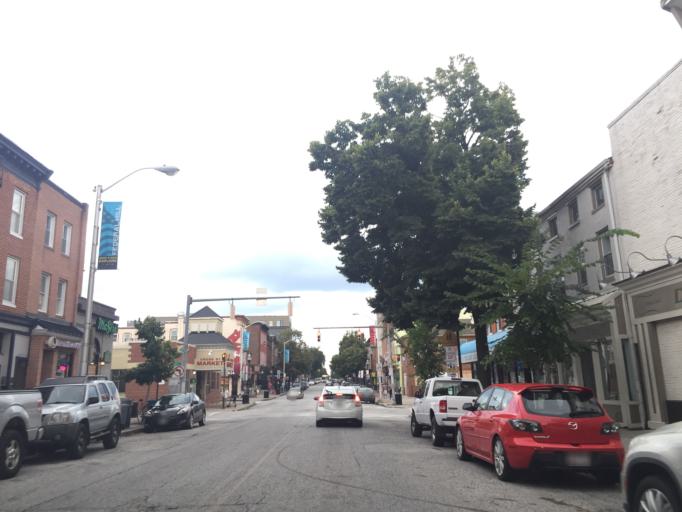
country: US
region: Maryland
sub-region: City of Baltimore
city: Baltimore
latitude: 39.2772
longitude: -76.6144
